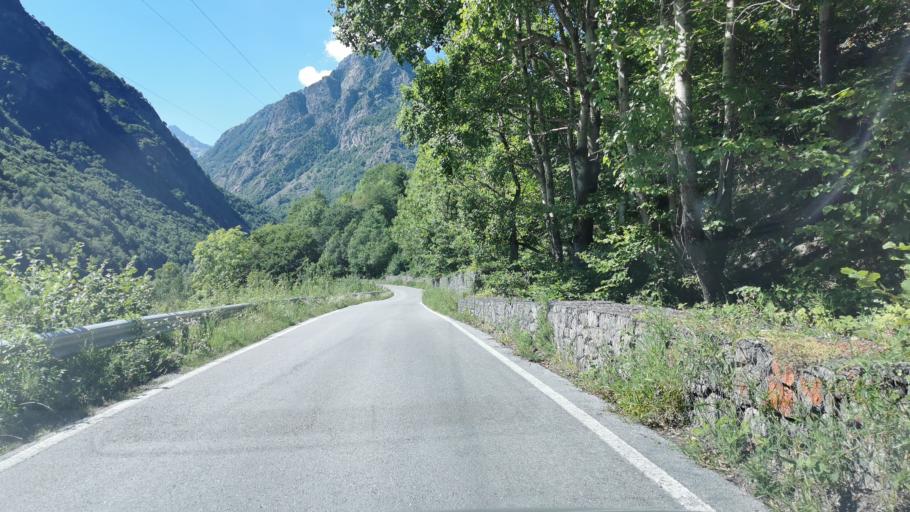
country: IT
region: Piedmont
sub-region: Provincia di Cuneo
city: Entracque
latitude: 44.2196
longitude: 7.3864
